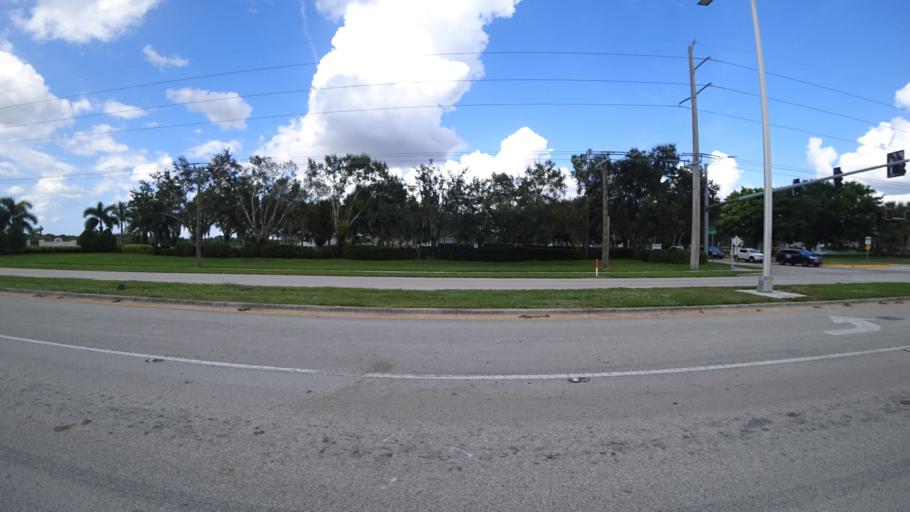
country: US
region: Florida
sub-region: Manatee County
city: Bayshore Gardens
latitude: 27.4478
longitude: -82.6077
